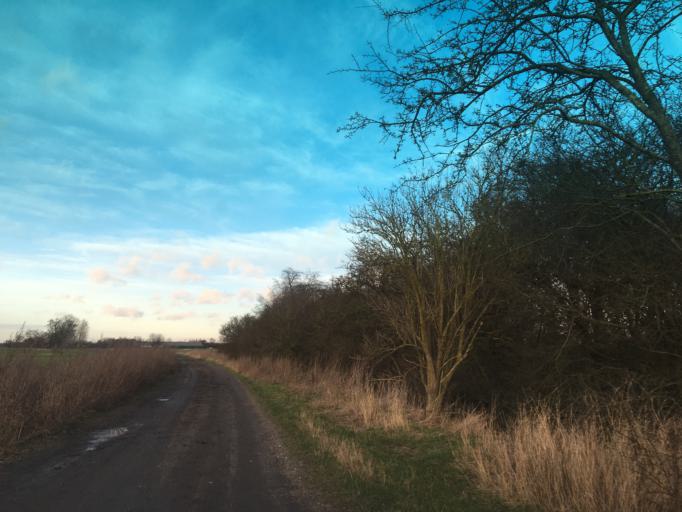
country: DK
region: Capital Region
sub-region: Tarnby Kommune
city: Tarnby
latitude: 55.5907
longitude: 12.6189
